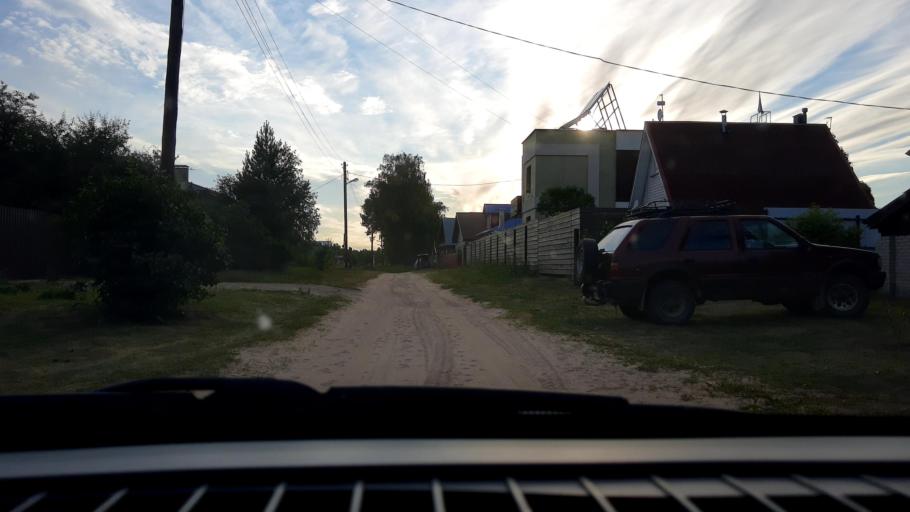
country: RU
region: Nizjnij Novgorod
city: Kstovo
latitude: 56.2646
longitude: 44.3004
